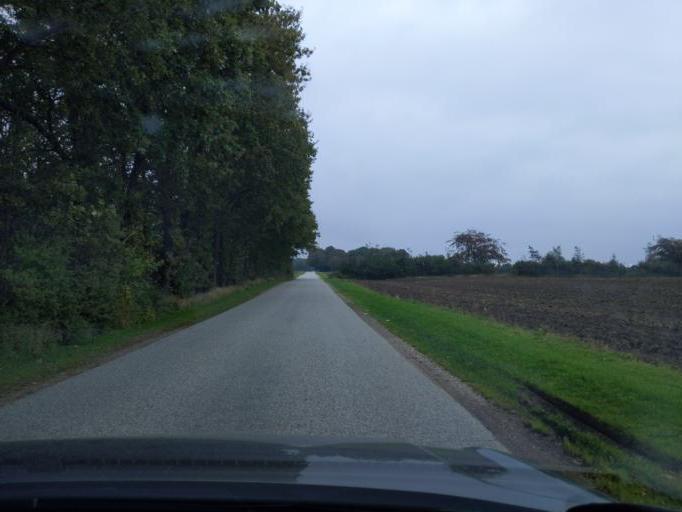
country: DK
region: Central Jutland
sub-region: Viborg Kommune
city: Karup
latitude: 56.3725
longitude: 9.2799
